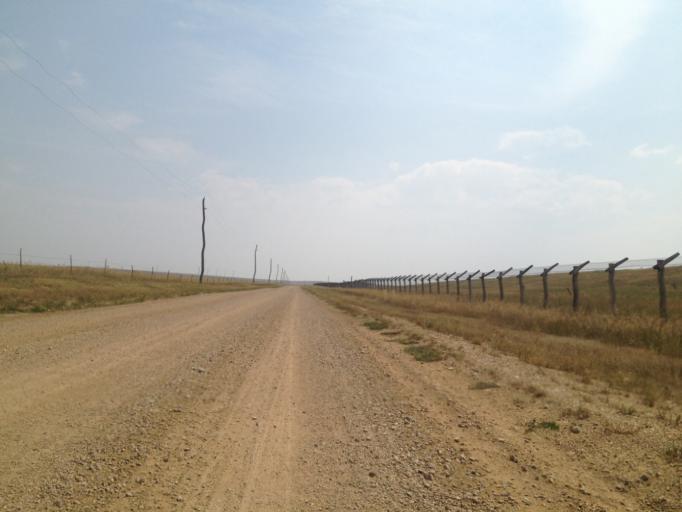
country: US
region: Colorado
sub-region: Boulder County
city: Superior
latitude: 39.9472
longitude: -105.1988
